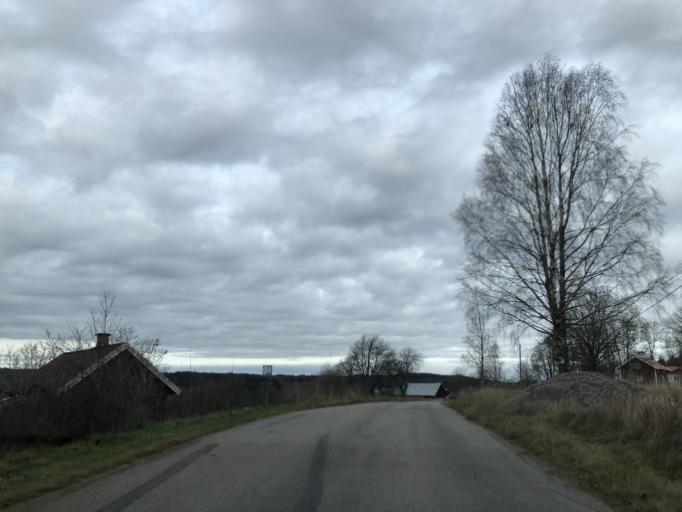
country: SE
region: Vaestra Goetaland
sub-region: Ulricehamns Kommun
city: Ulricehamn
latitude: 57.7197
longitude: 13.3593
